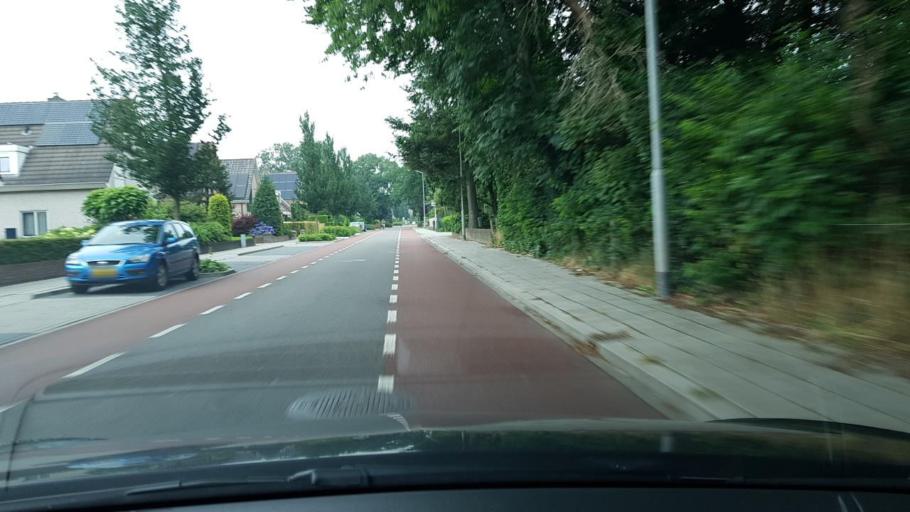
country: NL
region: Gelderland
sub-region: Gemeente Putten
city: Putten
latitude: 52.2510
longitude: 5.6151
